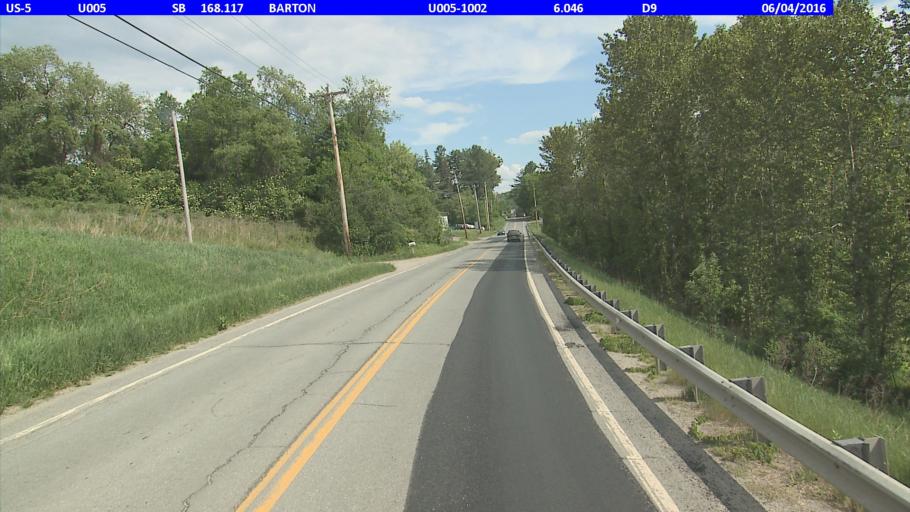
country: US
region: Vermont
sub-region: Orleans County
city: Newport
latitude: 44.7552
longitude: -72.1844
